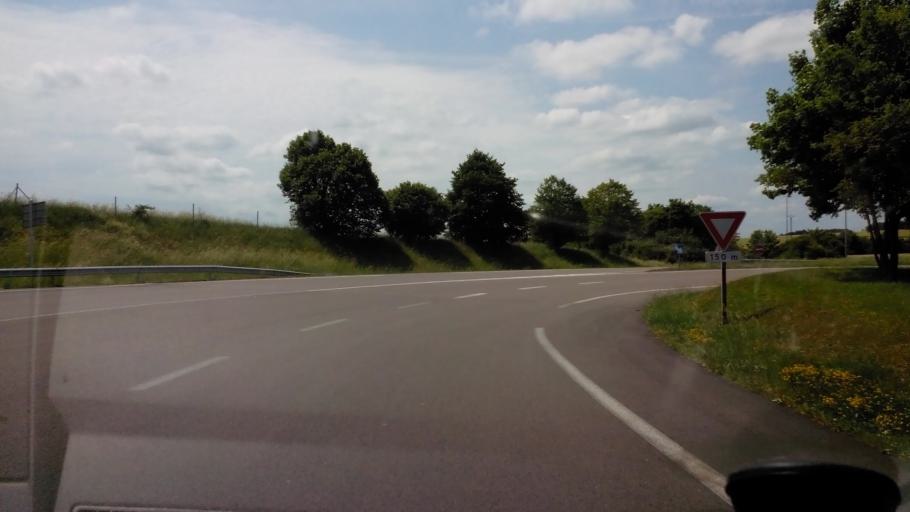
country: FR
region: Bourgogne
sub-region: Departement de la Cote-d'Or
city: Selongey
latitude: 47.5372
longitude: 5.1938
